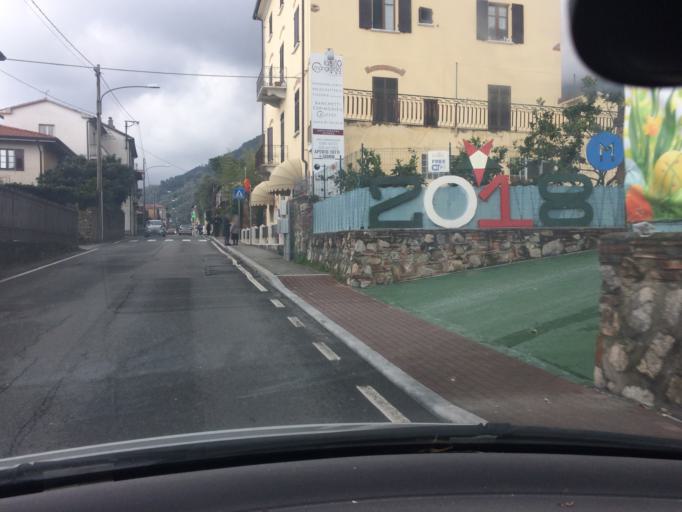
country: IT
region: Tuscany
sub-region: Provincia di Massa-Carrara
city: Massa
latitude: 44.0424
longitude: 10.1369
